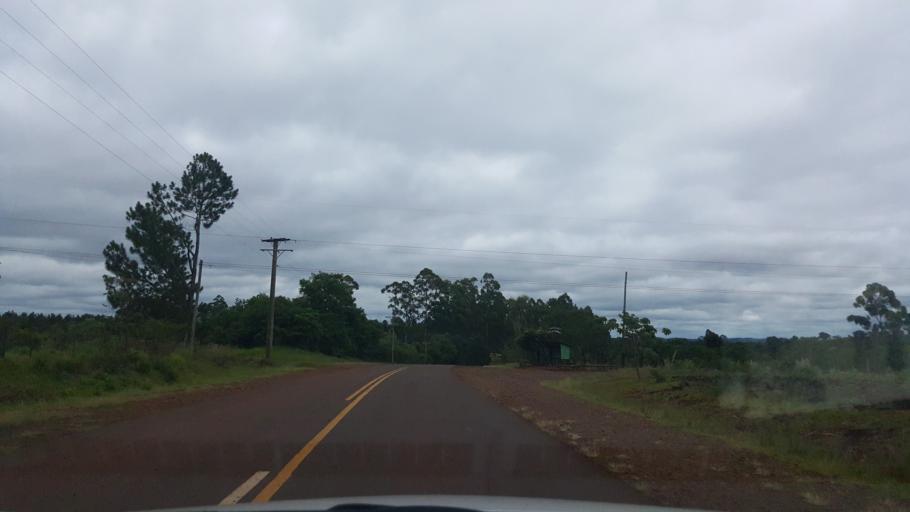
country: AR
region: Misiones
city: Ruiz de Montoya
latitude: -26.9686
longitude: -55.0801
